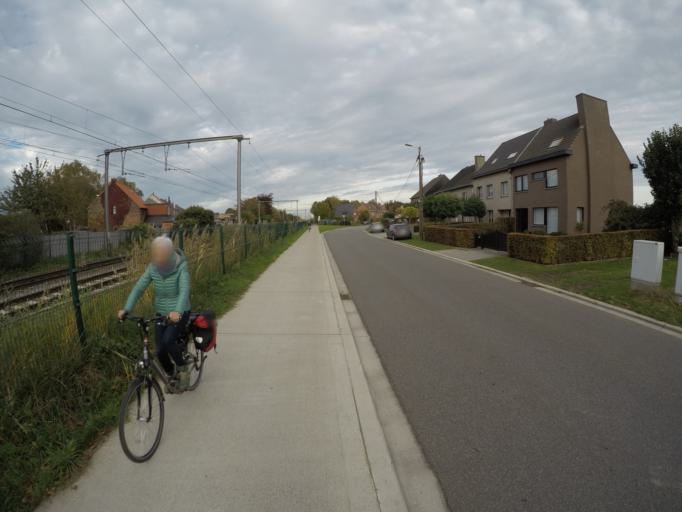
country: BE
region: Flanders
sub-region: Provincie Oost-Vlaanderen
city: Waasmunster
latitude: 51.1508
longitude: 4.0887
